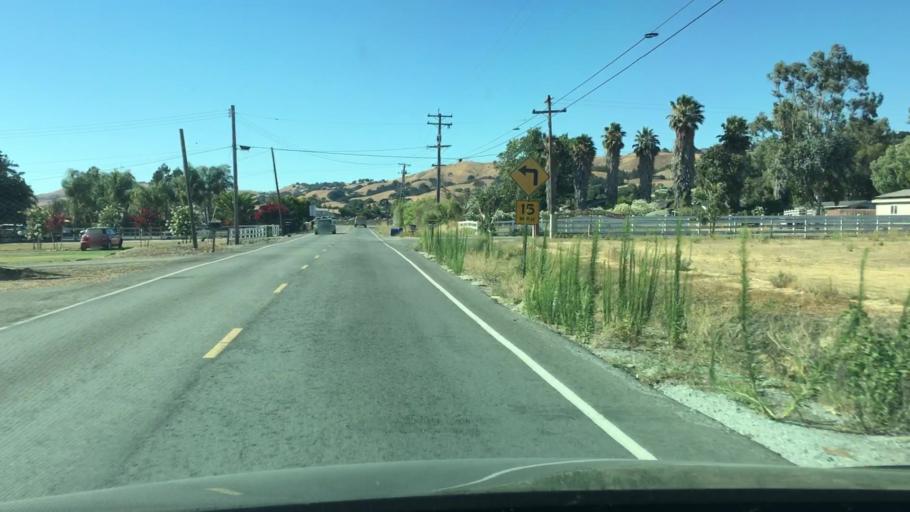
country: US
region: California
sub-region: Santa Clara County
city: San Martin
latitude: 37.1276
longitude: -121.5999
